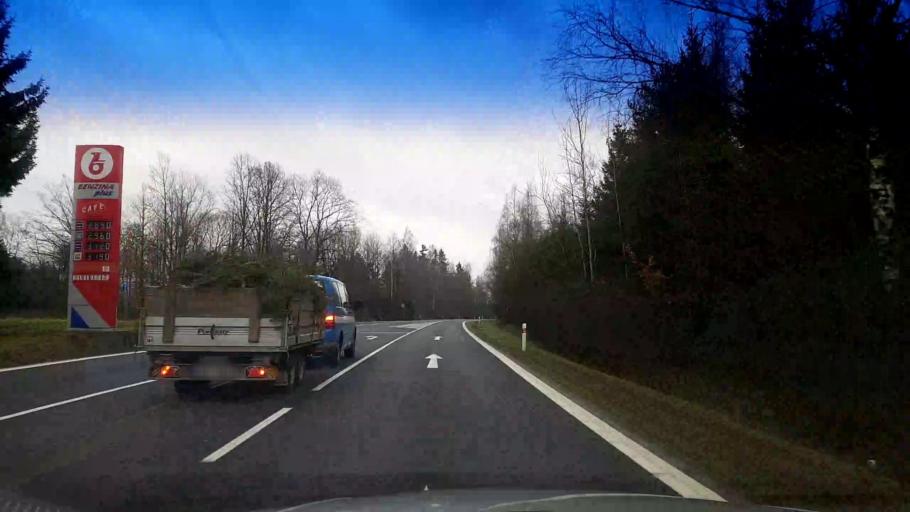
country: CZ
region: Karlovarsky
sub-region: Okres Cheb
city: Frantiskovy Lazne
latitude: 50.1228
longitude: 12.3673
